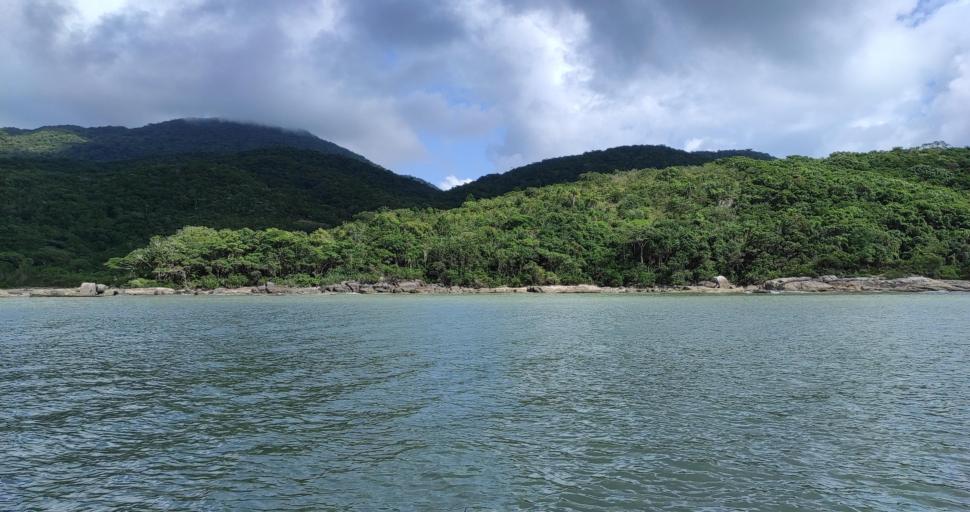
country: BR
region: Santa Catarina
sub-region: Porto Belo
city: Porto Belo
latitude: -27.1988
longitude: -48.5555
